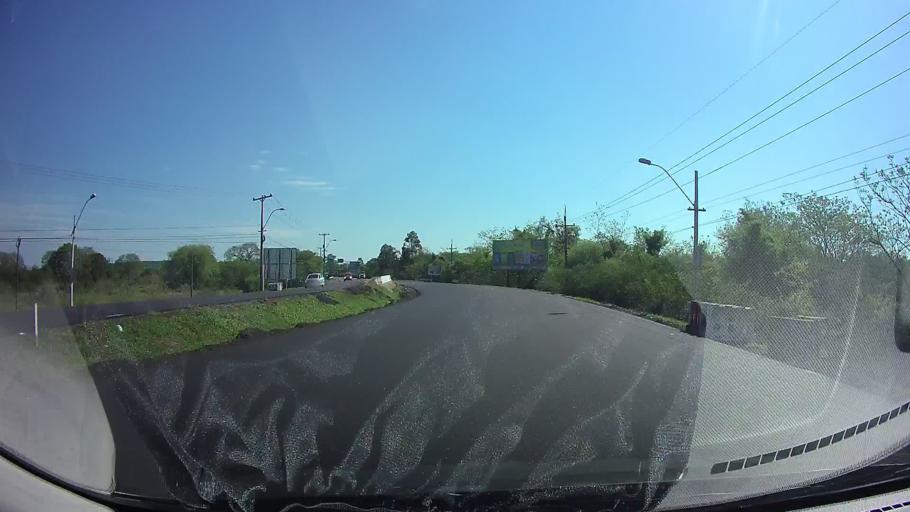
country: PY
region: Central
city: Ypacarai
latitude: -25.3897
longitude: -57.2729
